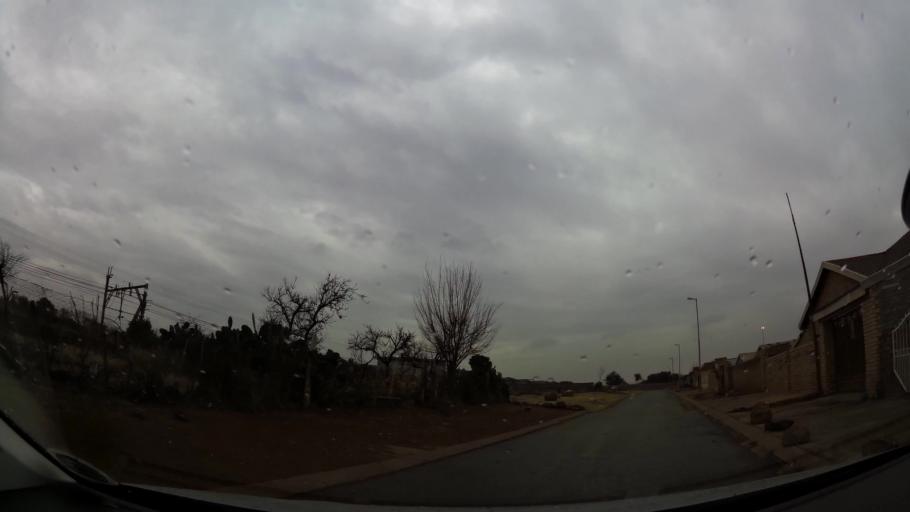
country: ZA
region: Gauteng
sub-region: City of Johannesburg Metropolitan Municipality
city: Soweto
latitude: -26.2467
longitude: 27.8659
